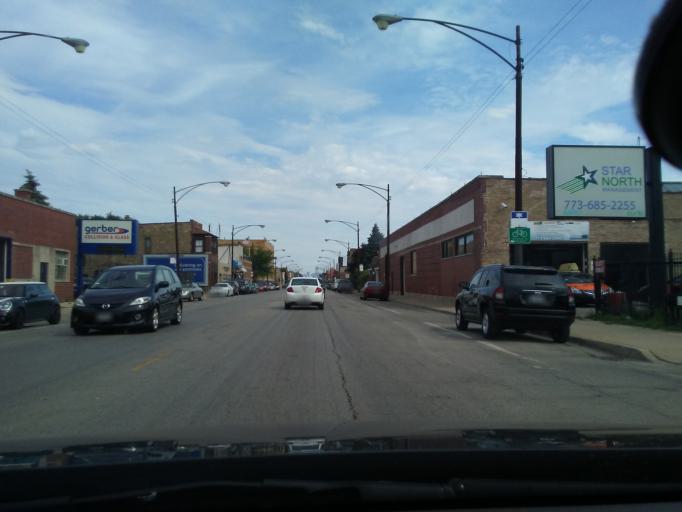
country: US
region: Illinois
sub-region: Cook County
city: Lincolnwood
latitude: 41.9634
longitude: -87.7333
